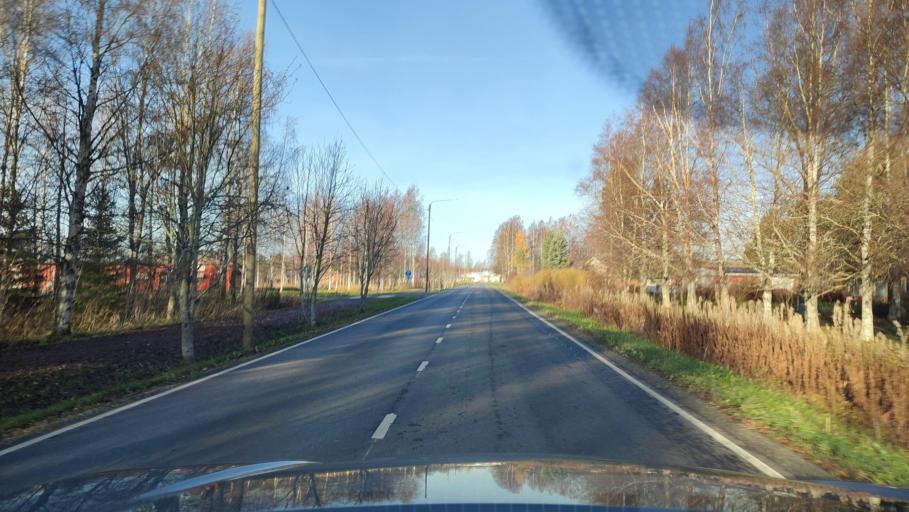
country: FI
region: Southern Ostrobothnia
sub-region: Suupohja
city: Karijoki
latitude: 62.3029
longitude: 21.7127
